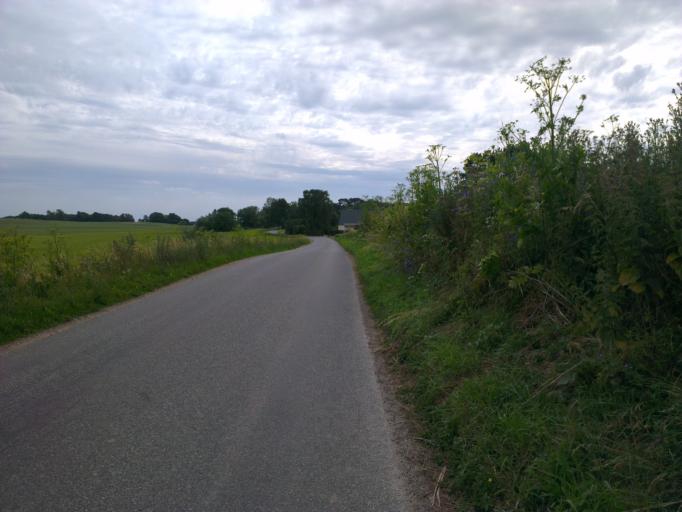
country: DK
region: Capital Region
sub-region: Frederikssund Kommune
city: Skibby
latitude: 55.7533
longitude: 12.0117
